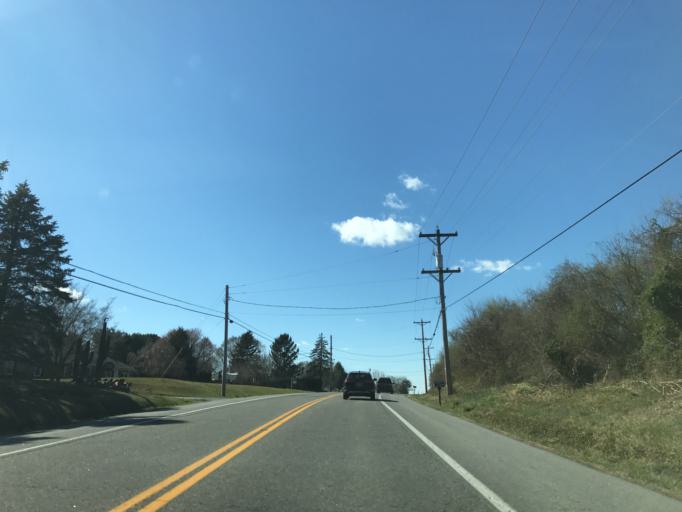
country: US
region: Maryland
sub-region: Kent County
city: Chestertown
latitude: 39.2179
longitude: -76.1330
